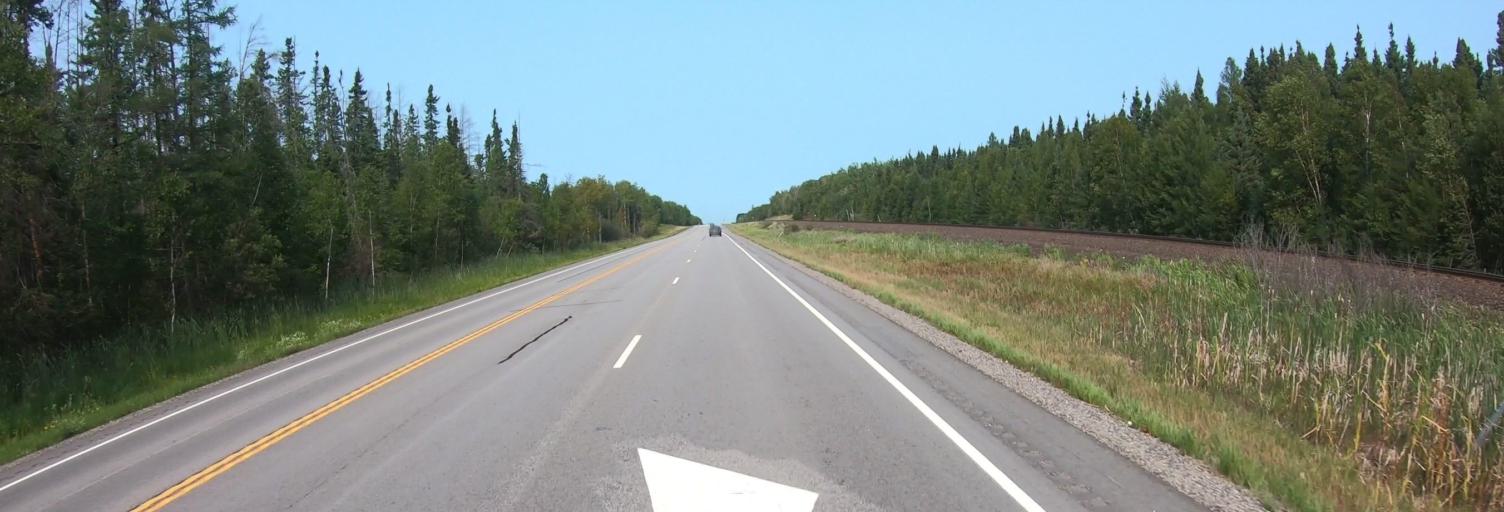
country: CA
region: Ontario
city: Fort Frances
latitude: 48.4587
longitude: -93.2829
